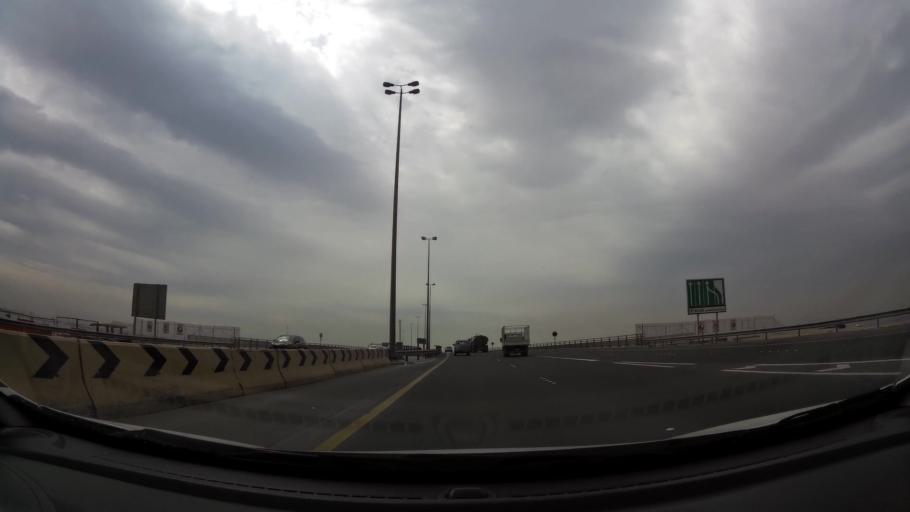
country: BH
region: Manama
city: Manama
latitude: 26.1953
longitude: 50.5895
